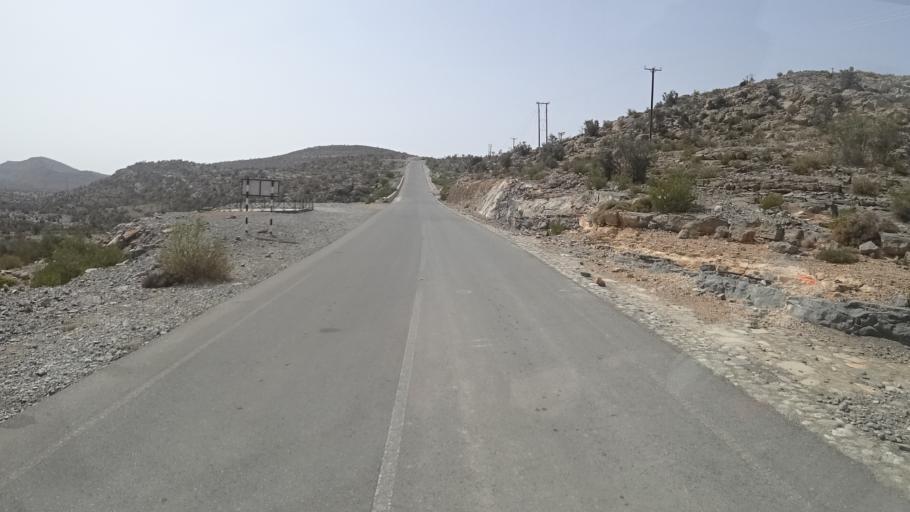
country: OM
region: Al Batinah
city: Bayt al `Awabi
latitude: 23.1565
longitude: 57.4228
